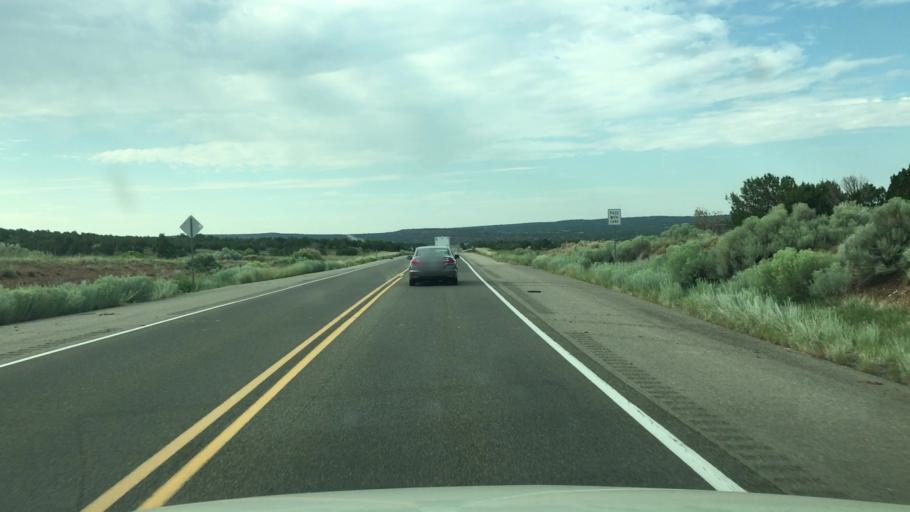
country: US
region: New Mexico
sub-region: Santa Fe County
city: Eldorado at Santa Fe
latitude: 35.2671
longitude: -105.8090
